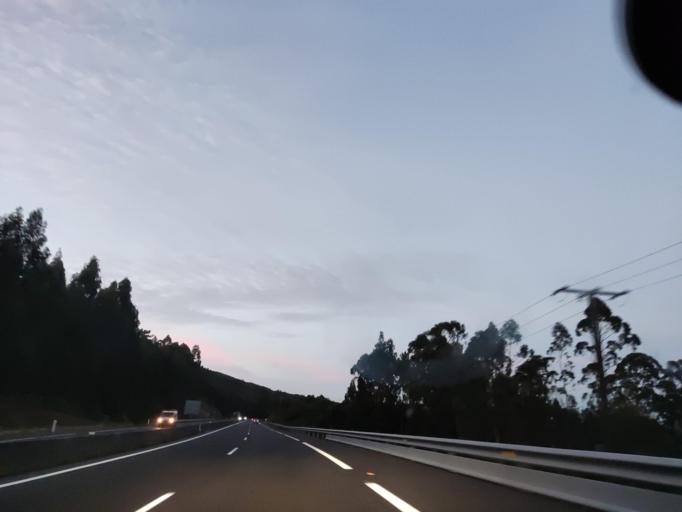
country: ES
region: Galicia
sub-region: Provincia da Coruna
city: Boiro
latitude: 42.6147
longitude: -8.9545
